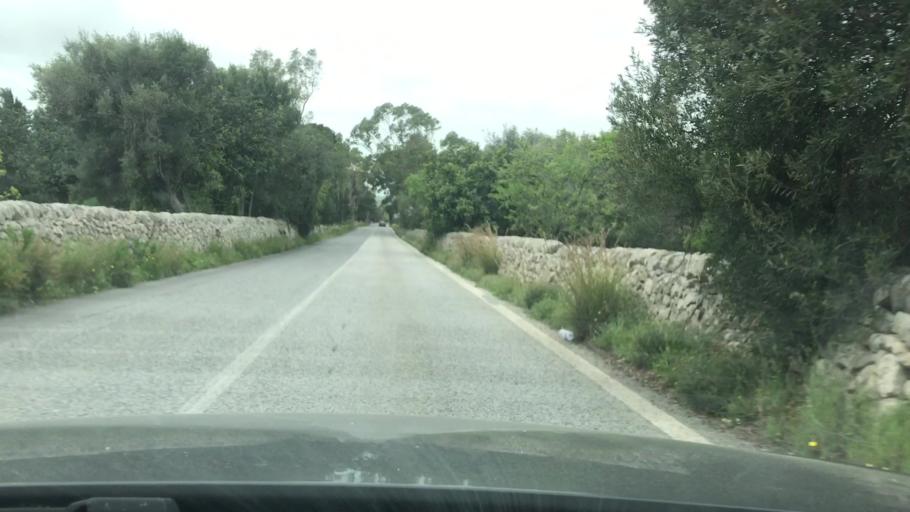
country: IT
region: Sicily
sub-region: Ragusa
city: Scicli
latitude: 36.7997
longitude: 14.7136
